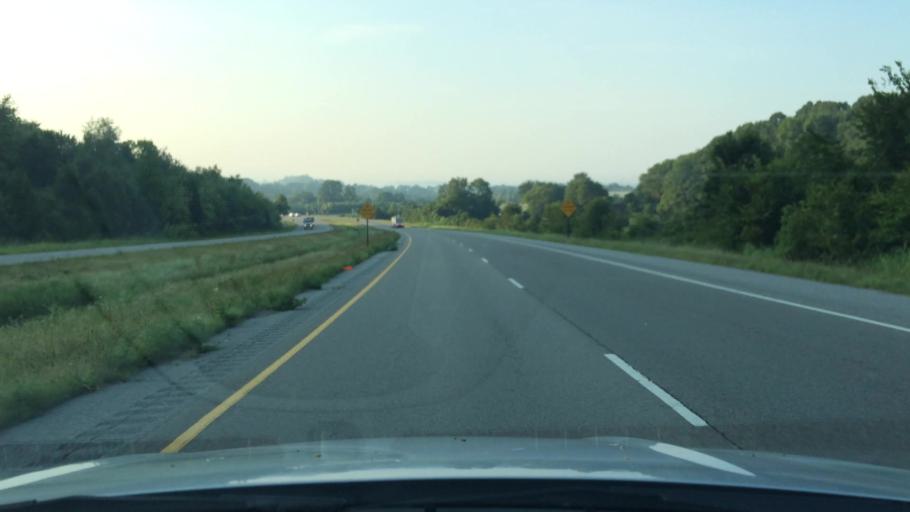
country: US
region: Tennessee
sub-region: Giles County
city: Pulaski
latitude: 35.1748
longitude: -87.0588
